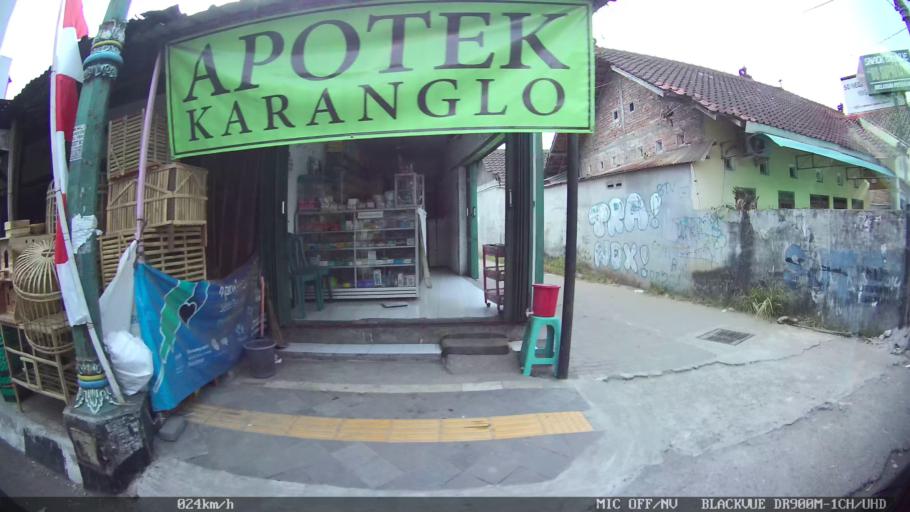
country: ID
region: Daerah Istimewa Yogyakarta
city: Yogyakarta
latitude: -7.8279
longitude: 110.4047
